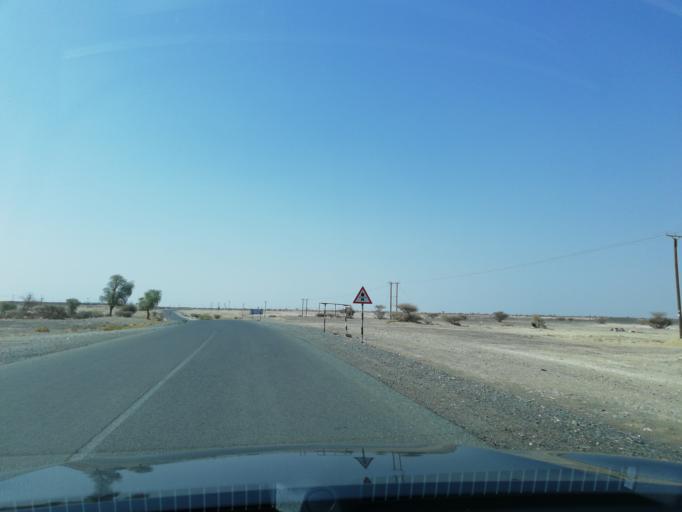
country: OM
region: Muhafazat ad Dakhiliyah
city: Adam
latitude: 22.3587
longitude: 58.0661
